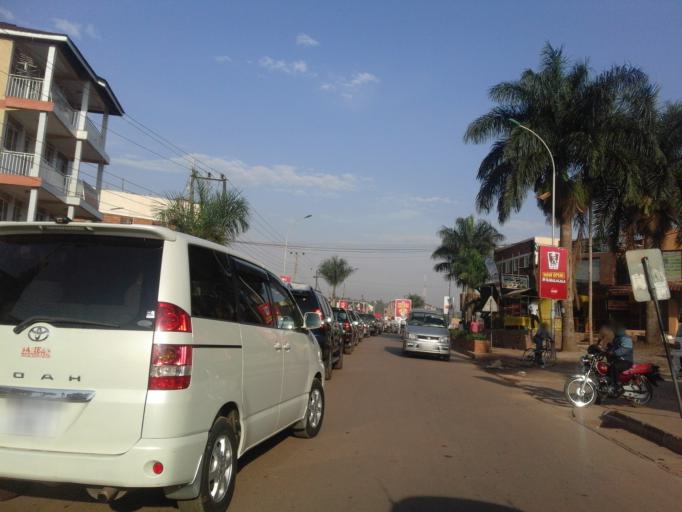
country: UG
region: Central Region
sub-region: Kampala District
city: Kampala
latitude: 0.2977
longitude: 32.6014
